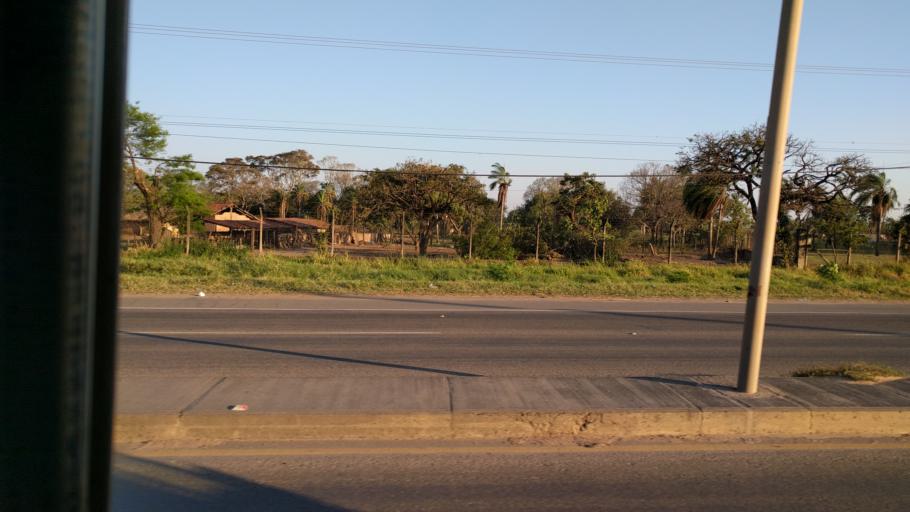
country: BO
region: Santa Cruz
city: Cotoca
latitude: -17.7623
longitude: -63.0260
